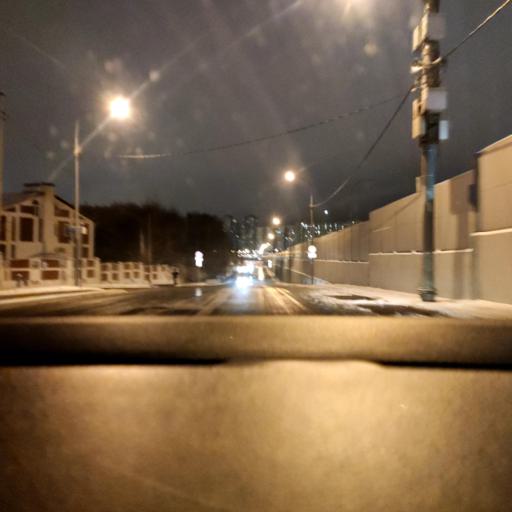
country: RU
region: Moskovskaya
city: Pavshino
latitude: 55.8612
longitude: 37.3610
